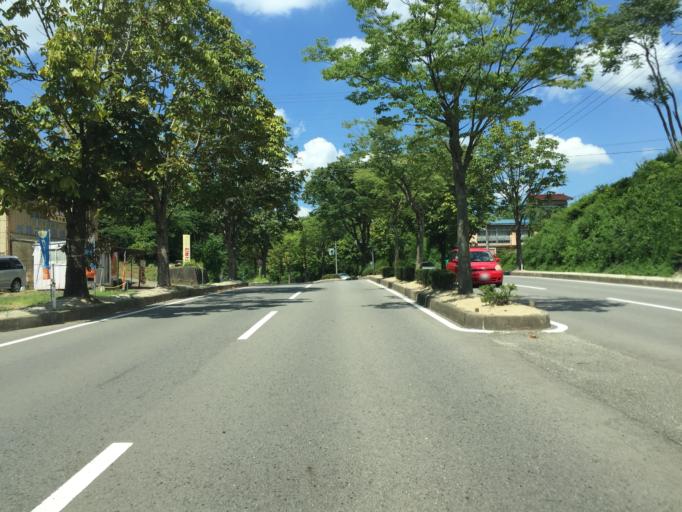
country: JP
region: Fukushima
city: Fukushima-shi
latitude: 37.7064
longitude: 140.4709
